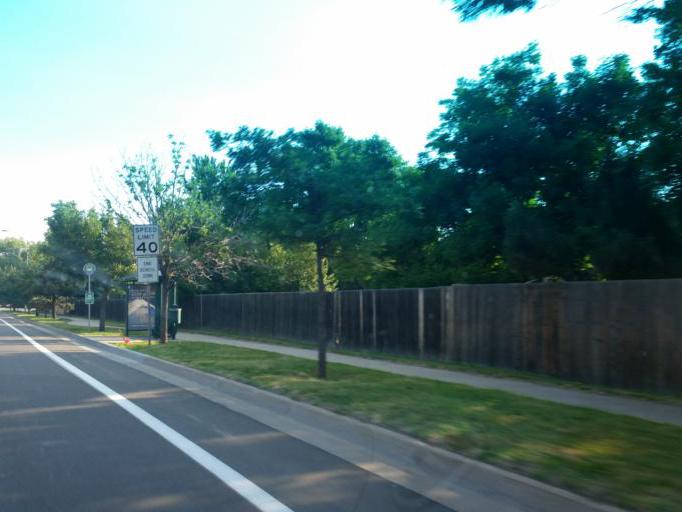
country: US
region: Colorado
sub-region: Larimer County
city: Fort Collins
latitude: 40.5607
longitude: -105.1151
